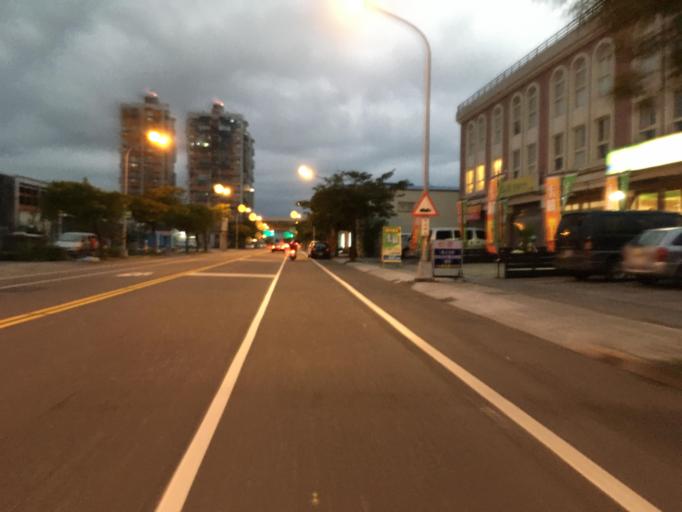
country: TW
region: Taiwan
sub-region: Yilan
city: Yilan
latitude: 24.6730
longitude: 121.7982
